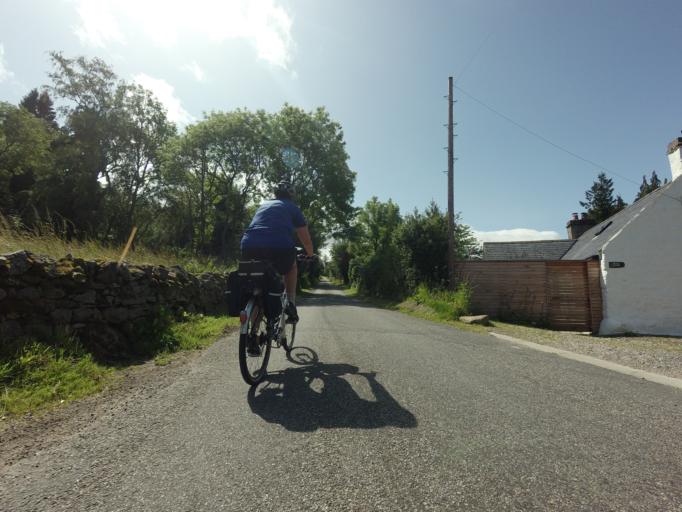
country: GB
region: Scotland
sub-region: Highland
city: Nairn
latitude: 57.5021
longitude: -3.9980
